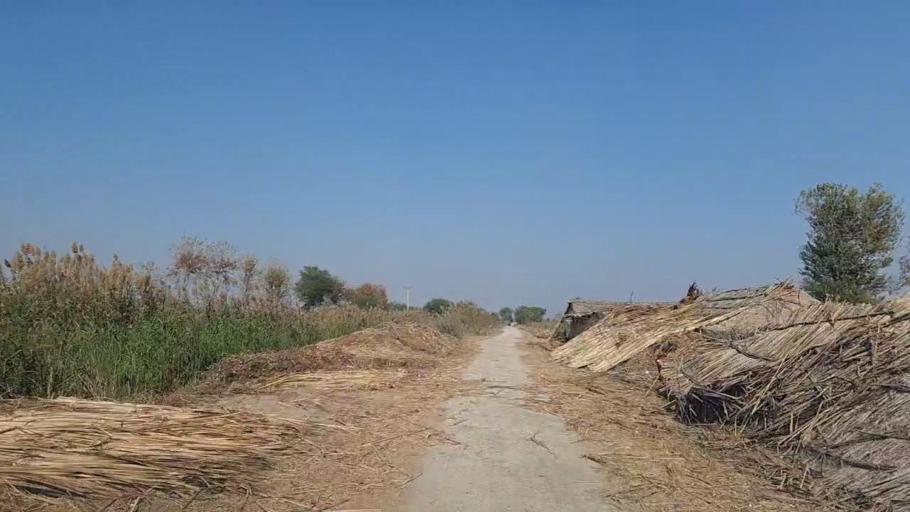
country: PK
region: Sindh
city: Daur
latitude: 26.5067
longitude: 68.3464
